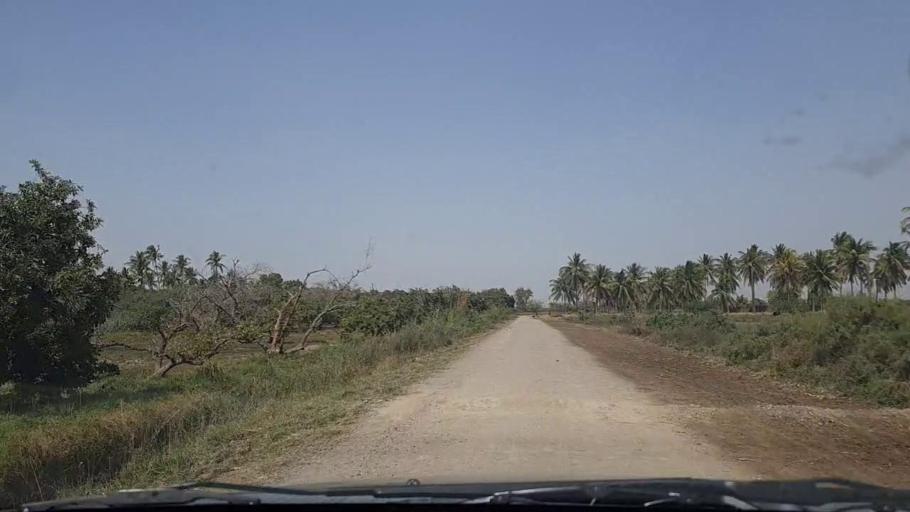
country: PK
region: Sindh
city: Keti Bandar
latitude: 24.2825
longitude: 67.6727
